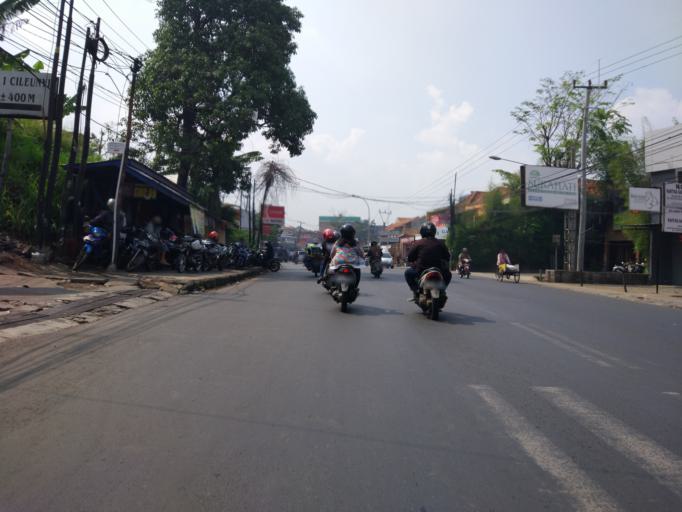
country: ID
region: West Java
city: Cileunyi
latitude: -6.9388
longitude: 107.7368
